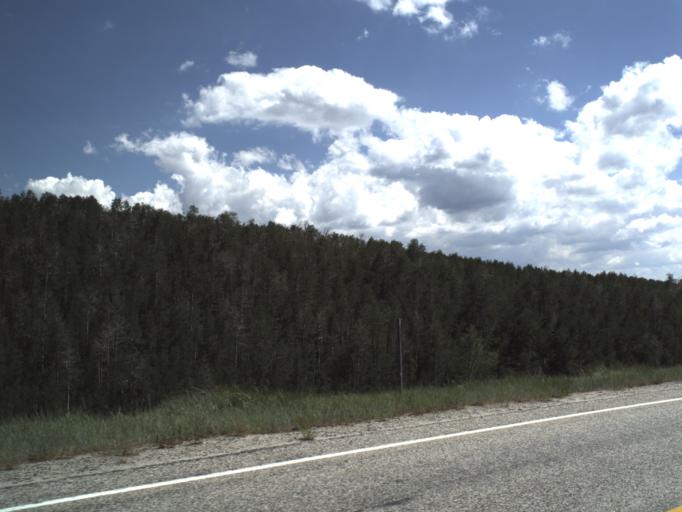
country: US
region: Utah
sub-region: Weber County
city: Wolf Creek
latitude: 41.4070
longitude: -111.5395
